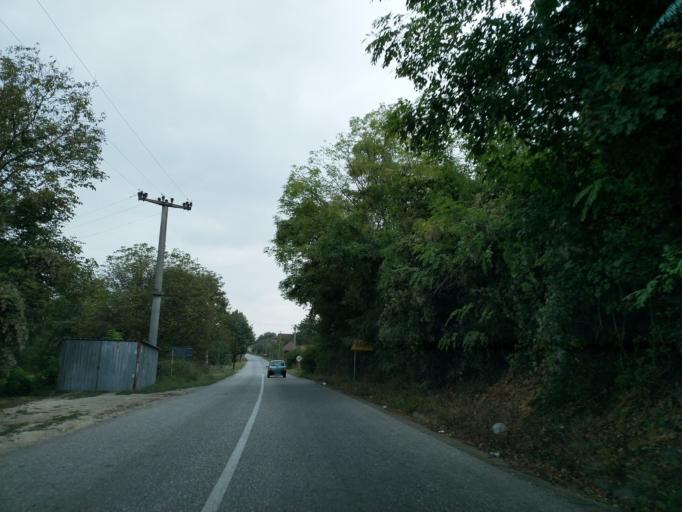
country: RS
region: Central Serbia
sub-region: Pomoravski Okrug
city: Jagodina
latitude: 44.0599
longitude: 21.1822
